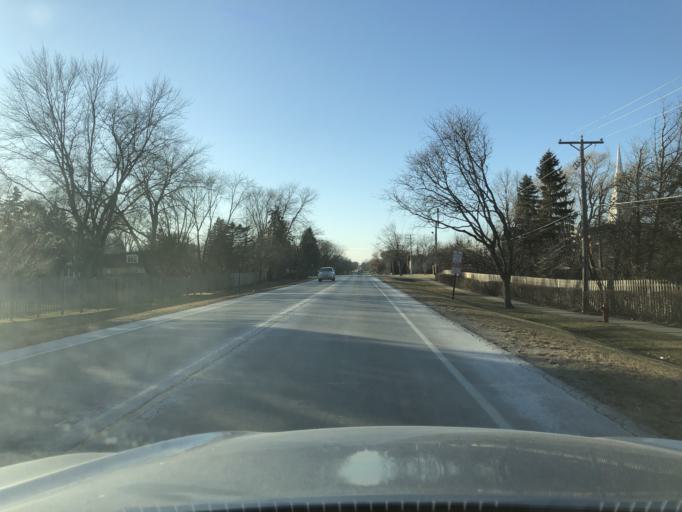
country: US
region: Illinois
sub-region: Lake County
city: Deer Park
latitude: 42.1541
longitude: -88.1053
